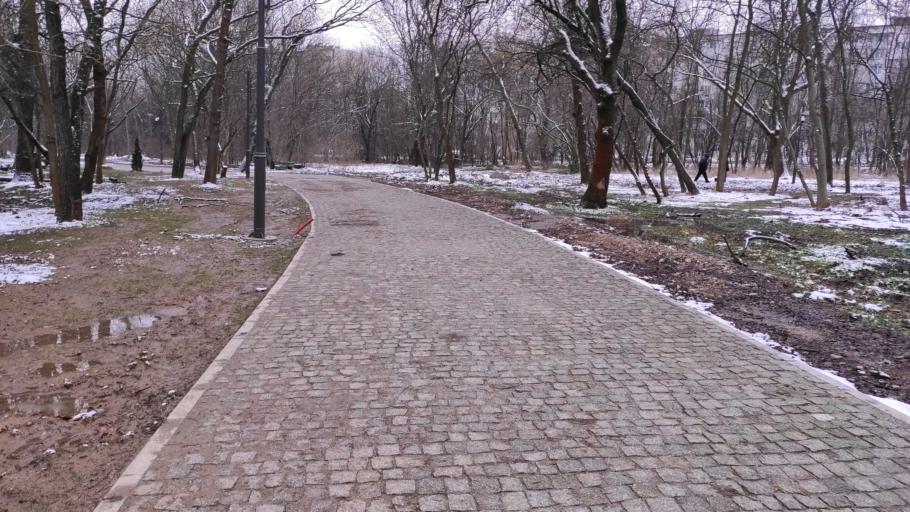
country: BG
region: Sofia-Capital
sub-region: Stolichna Obshtina
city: Sofia
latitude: 42.7100
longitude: 23.2776
